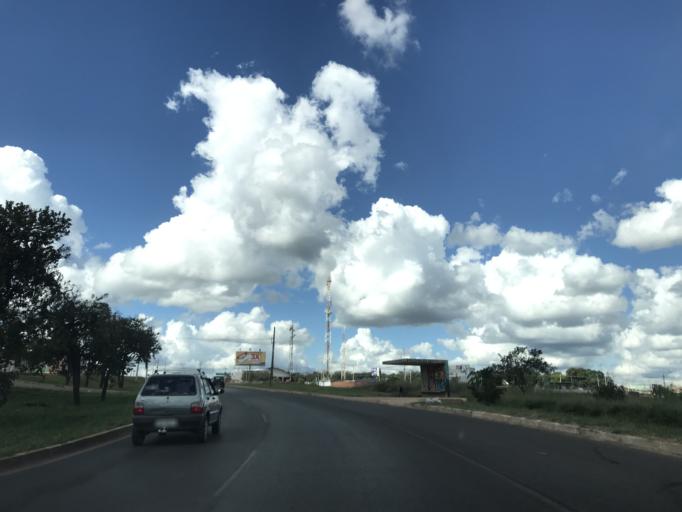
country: BR
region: Federal District
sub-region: Brasilia
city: Brasilia
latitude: -15.7617
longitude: -47.7869
